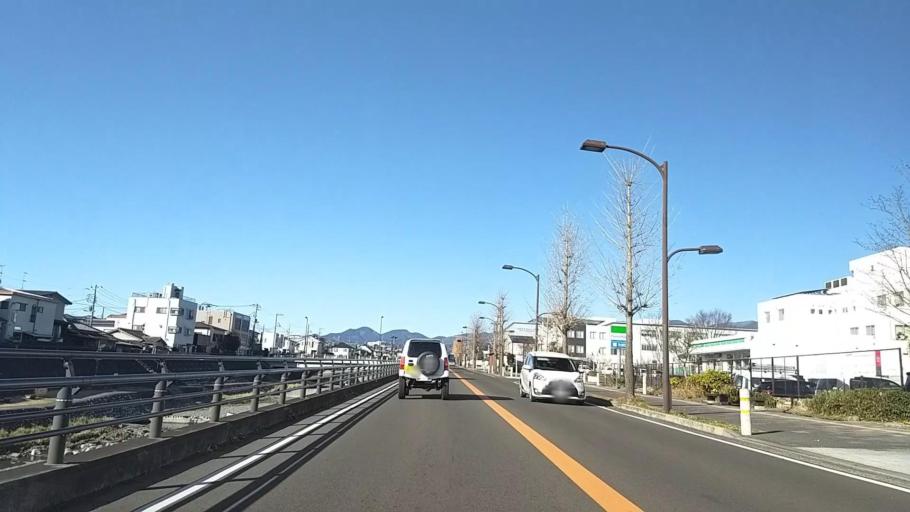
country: JP
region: Kanagawa
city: Hadano
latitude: 35.3743
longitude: 139.2198
